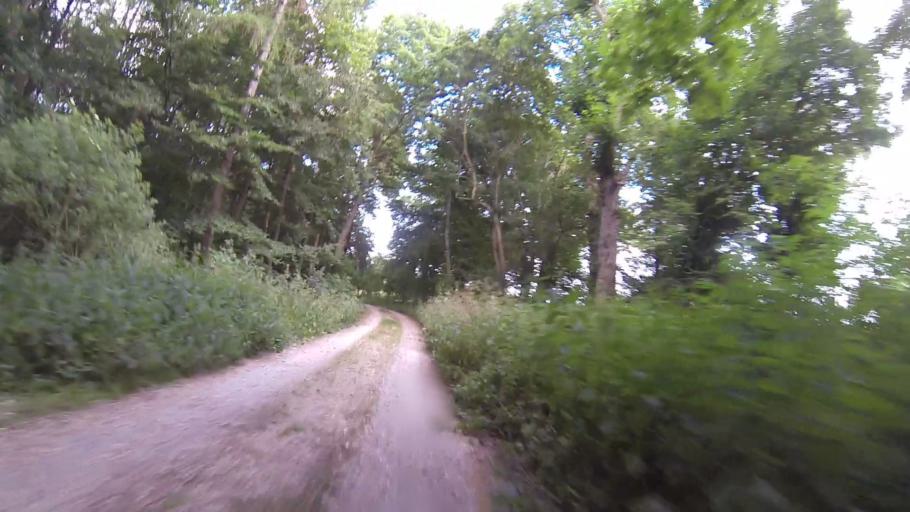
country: DE
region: Baden-Wuerttemberg
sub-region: Tuebingen Region
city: Blaubeuren
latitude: 48.4435
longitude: 9.8587
